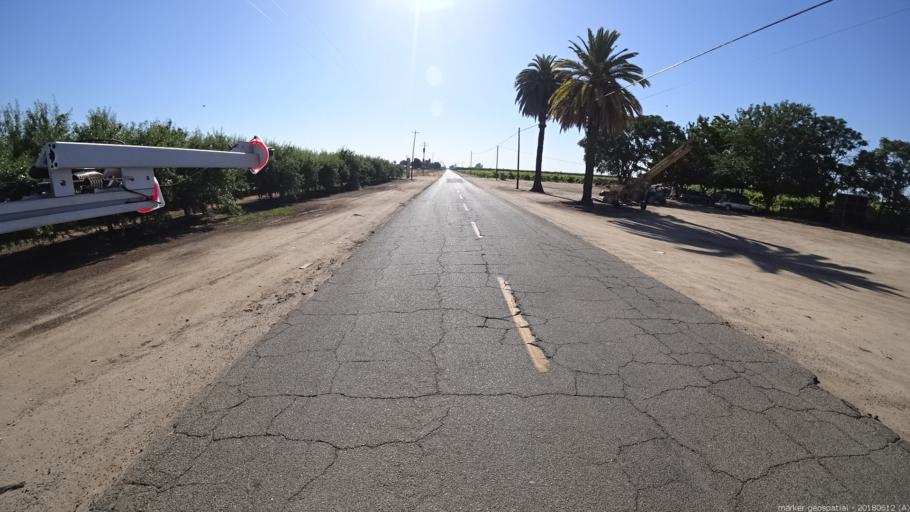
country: US
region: California
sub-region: Madera County
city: Fairmead
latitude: 37.0110
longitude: -120.1525
